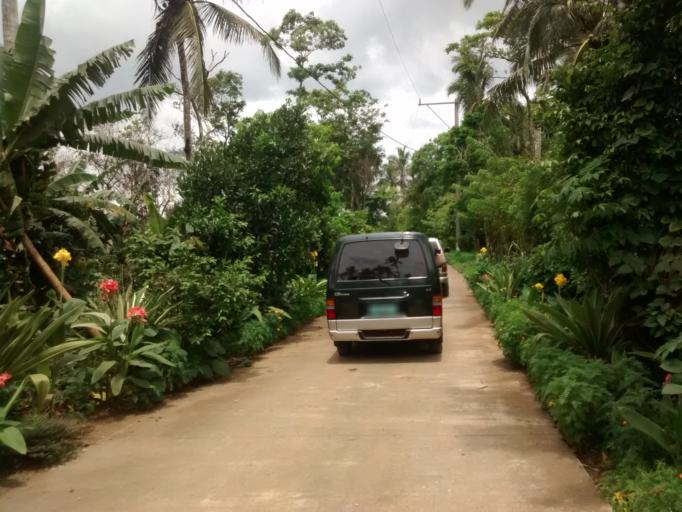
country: PH
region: Calabarzon
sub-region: Province of Quezon
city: Lucban
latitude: 14.1570
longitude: 121.5519
